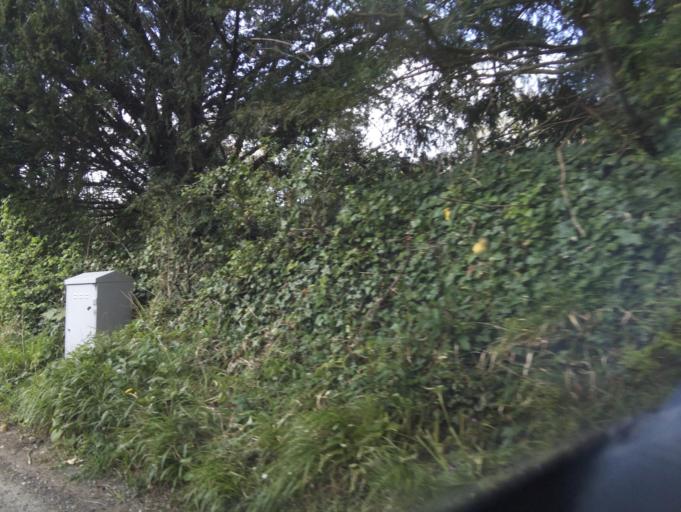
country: GB
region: England
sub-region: Hampshire
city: Romsey
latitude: 51.0352
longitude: -1.5089
